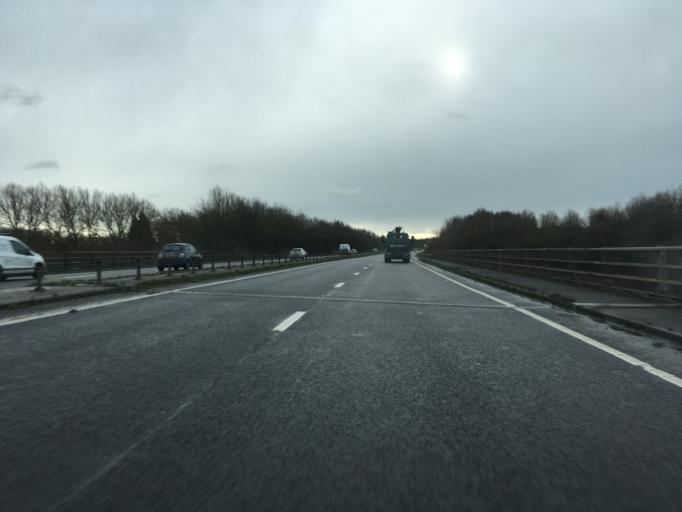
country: GB
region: England
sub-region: Warwickshire
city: Alcester
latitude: 52.1918
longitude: -1.8764
